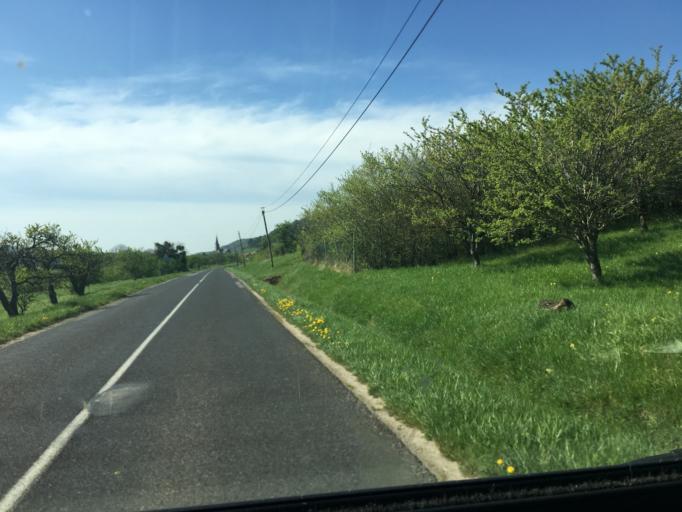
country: FR
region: Lorraine
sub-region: Departement de la Meuse
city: Vigneulles-les-Hattonchatel
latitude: 48.9026
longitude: 5.6632
